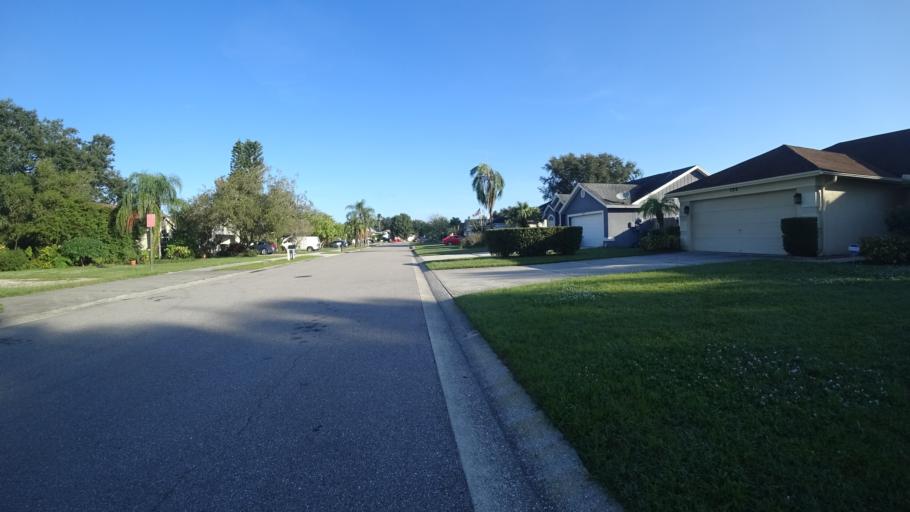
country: US
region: Florida
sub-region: Manatee County
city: Ellenton
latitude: 27.4924
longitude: -82.5032
